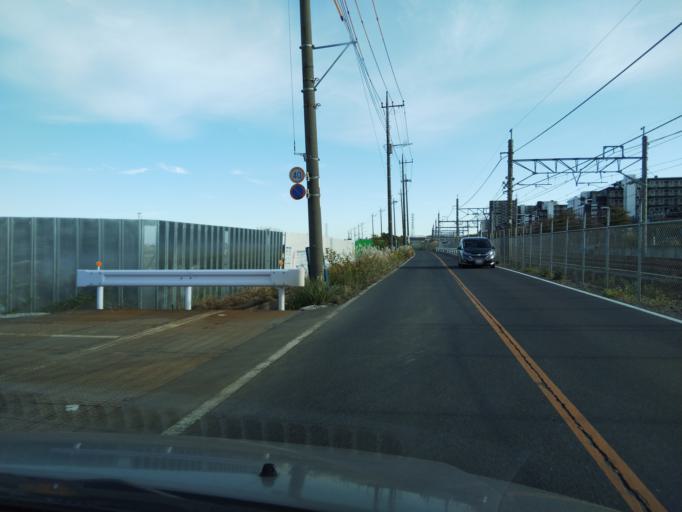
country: JP
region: Saitama
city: Yoshikawa
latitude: 35.8719
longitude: 139.8532
